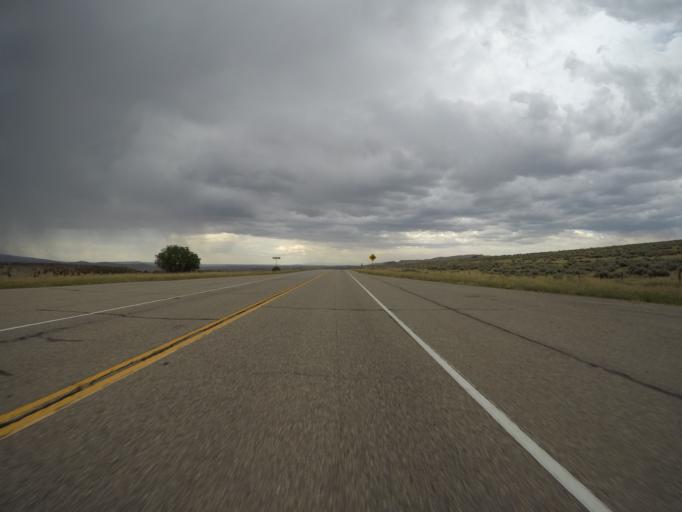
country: US
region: Colorado
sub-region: Rio Blanco County
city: Rangely
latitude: 40.3740
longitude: -108.3782
